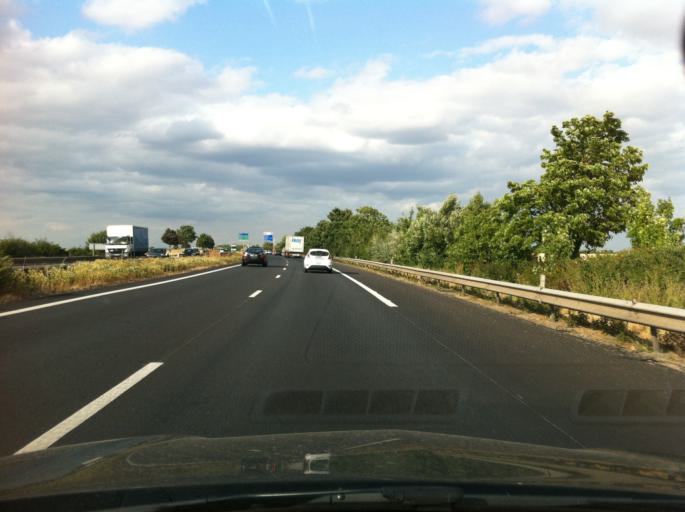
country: FR
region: Ile-de-France
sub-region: Departement de Seine-et-Marne
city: Moissy-Cramayel
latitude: 48.6492
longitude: 2.6096
